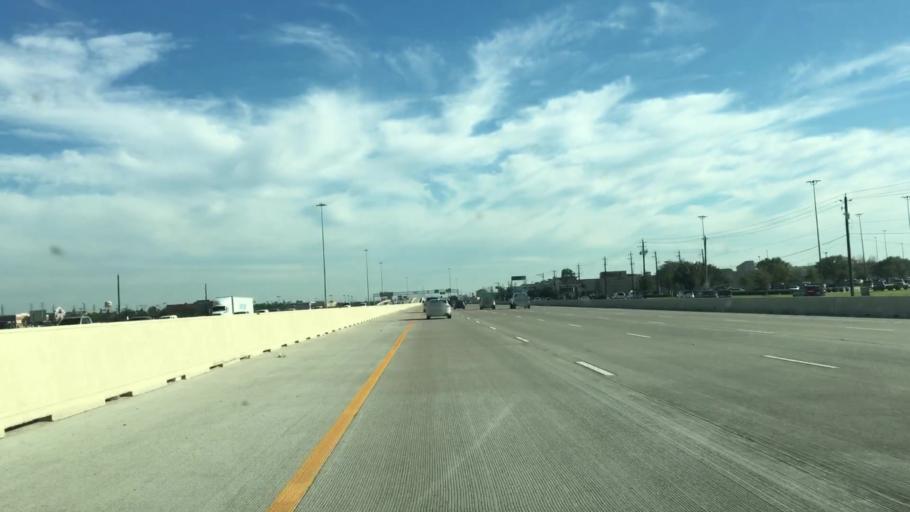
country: US
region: Texas
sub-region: Harris County
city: Webster
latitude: 29.5476
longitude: -95.1486
